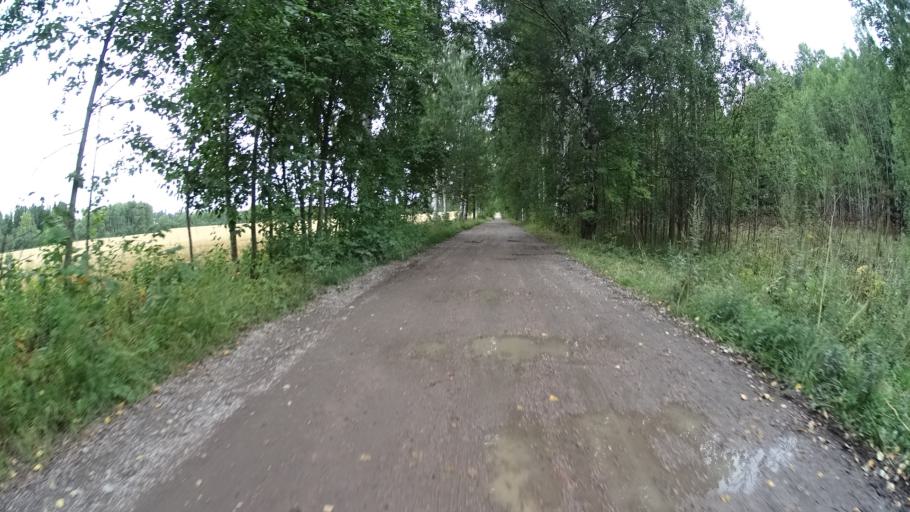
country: FI
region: Uusimaa
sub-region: Helsinki
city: Teekkarikylae
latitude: 60.2705
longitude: 24.8888
